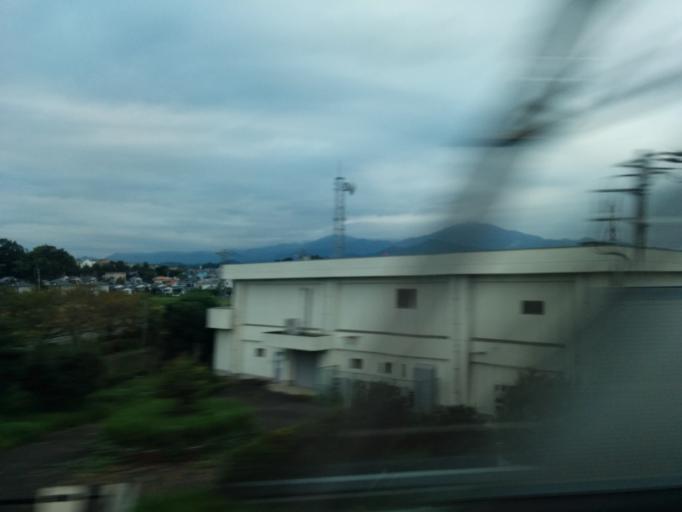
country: JP
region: Kanagawa
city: Hiratsuka
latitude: 35.3426
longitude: 139.3077
